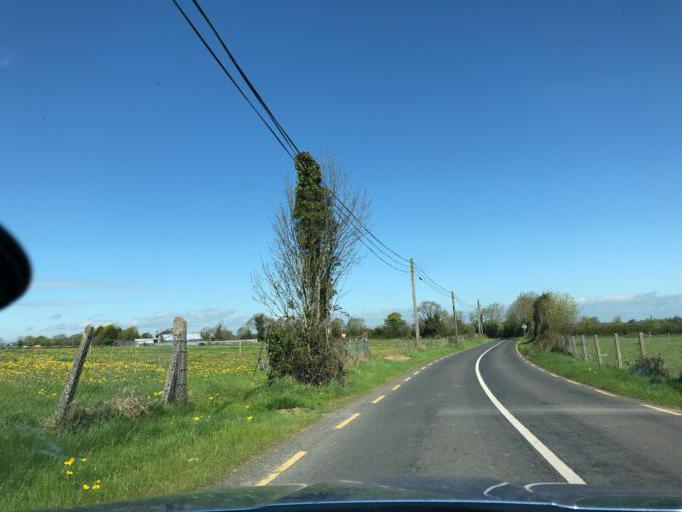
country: IE
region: Connaught
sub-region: County Galway
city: Portumna
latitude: 53.1240
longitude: -8.3339
